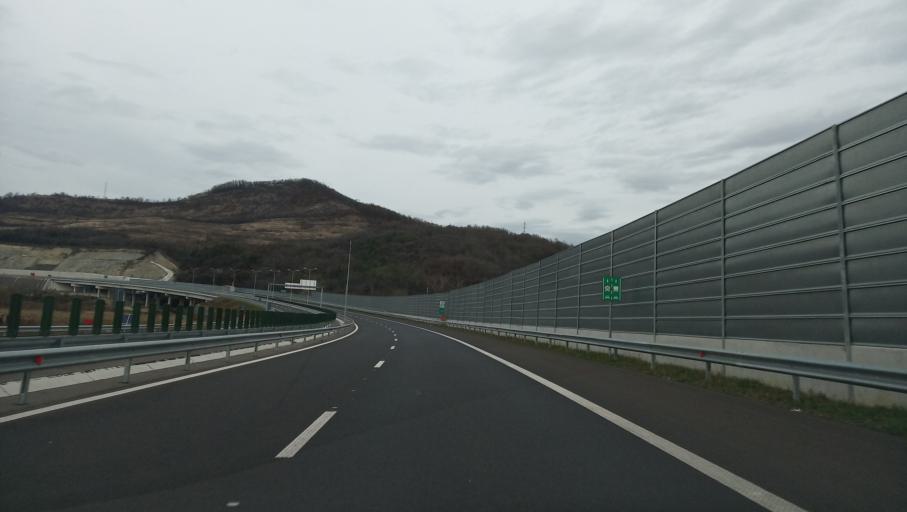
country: RO
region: Hunedoara
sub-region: Comuna Soimus
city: Soimus
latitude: 45.9215
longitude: 22.8724
